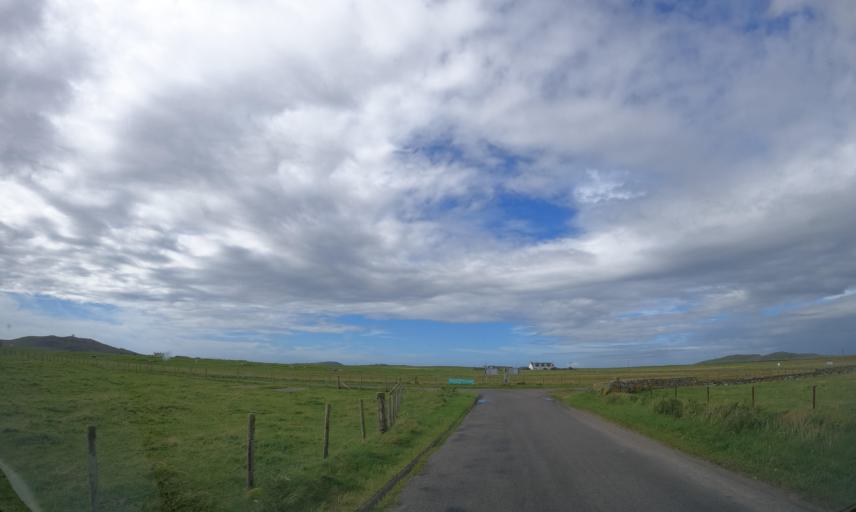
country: GB
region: Scotland
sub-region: Eilean Siar
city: Barra
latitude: 56.4838
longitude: -6.9008
